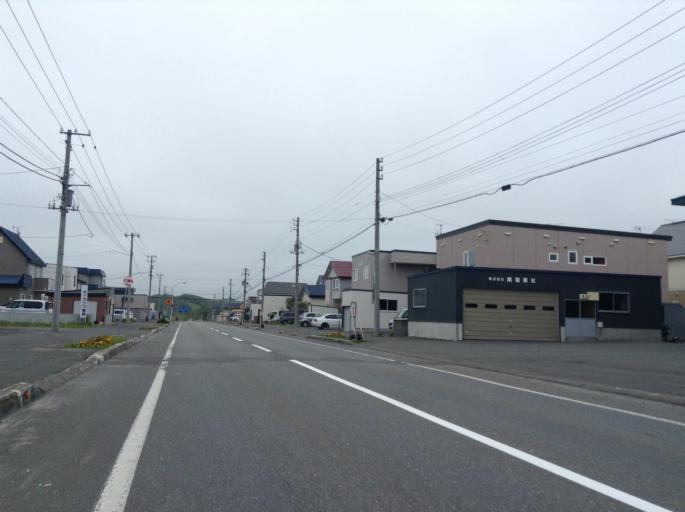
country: JP
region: Hokkaido
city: Wakkanai
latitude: 45.3895
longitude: 141.6927
